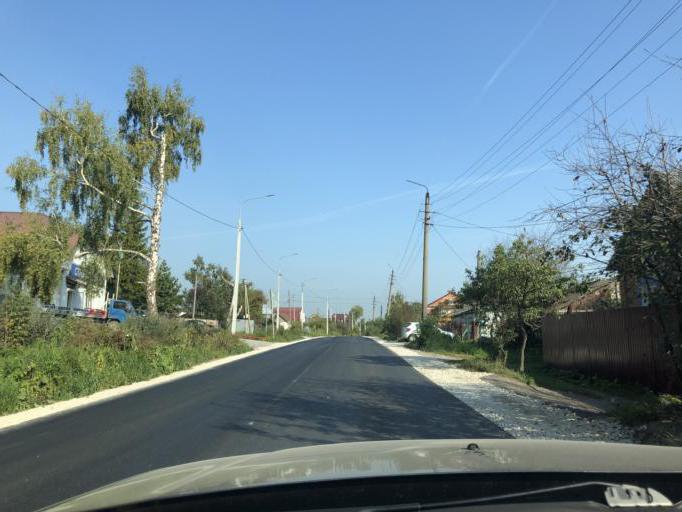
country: RU
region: Tula
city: Leninskiy
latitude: 54.2886
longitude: 37.4655
